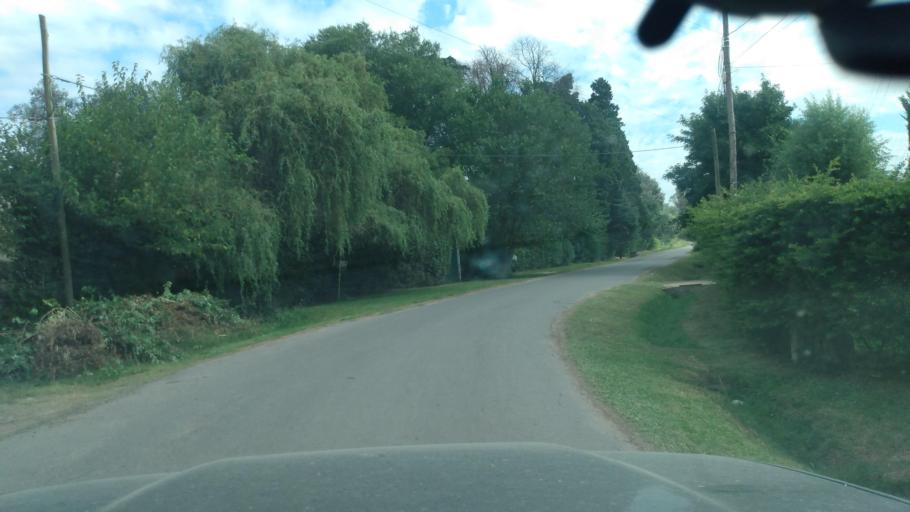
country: AR
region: Buenos Aires
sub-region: Partido de Lujan
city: Lujan
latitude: -34.5878
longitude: -59.0517
